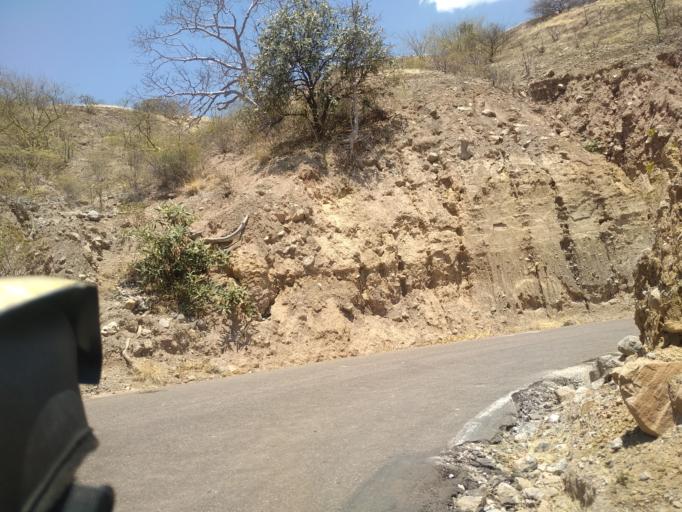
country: PE
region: Amazonas
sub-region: Provincia de Chachapoyas
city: Balsas
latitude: -6.8538
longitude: -78.0332
